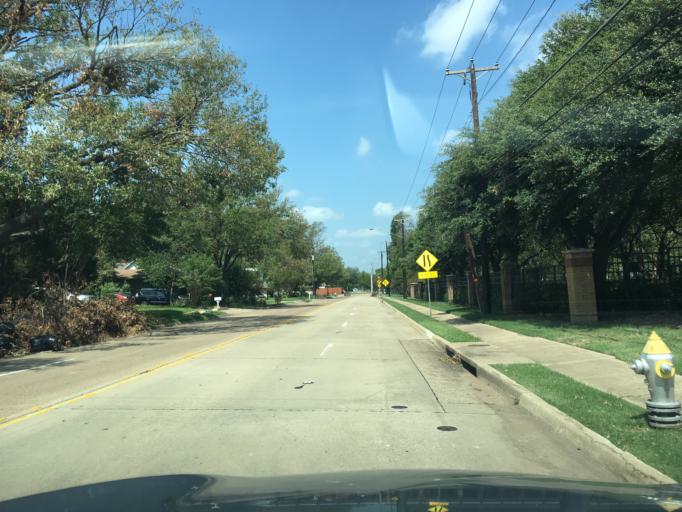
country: US
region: Texas
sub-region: Dallas County
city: Richardson
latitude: 32.9049
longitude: -96.7580
